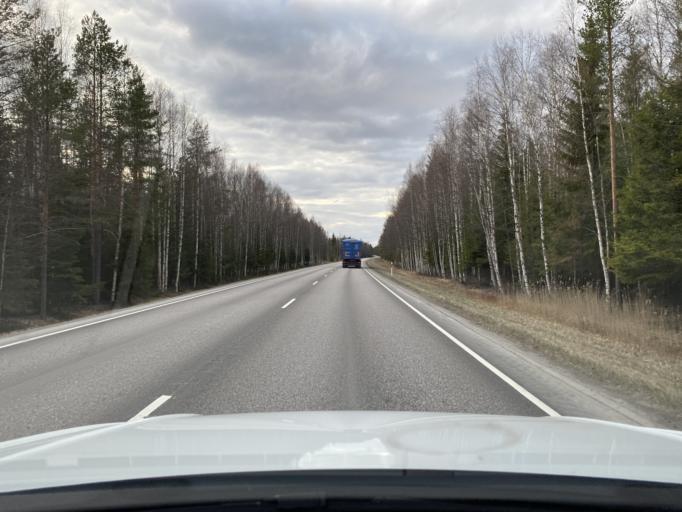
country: FI
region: Uusimaa
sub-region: Helsinki
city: Kaerkoelae
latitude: 60.8115
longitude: 24.0557
